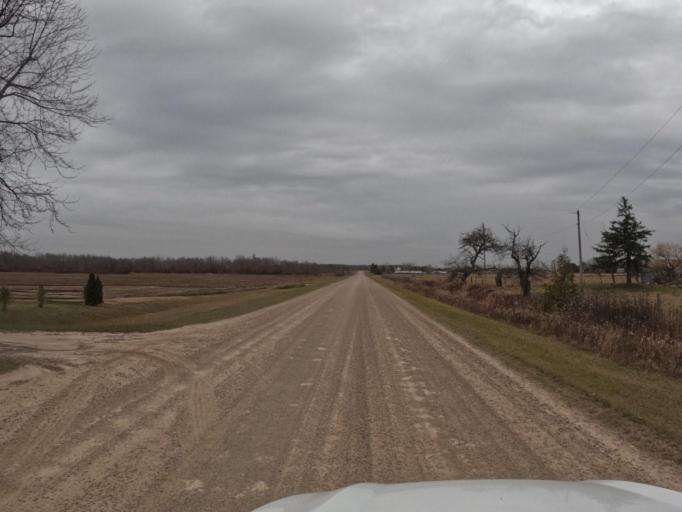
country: CA
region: Ontario
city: Shelburne
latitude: 43.8771
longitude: -80.3571
